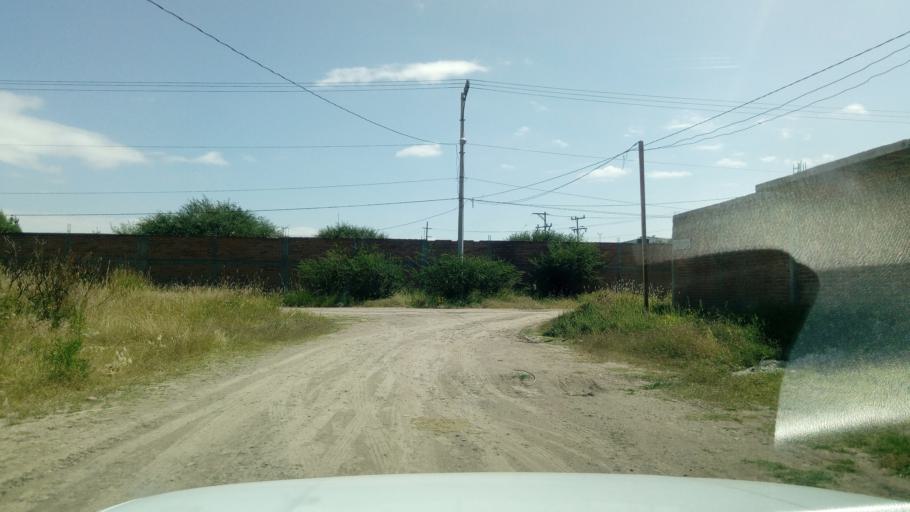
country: MX
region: Durango
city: Victoria de Durango
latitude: 23.9822
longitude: -104.6712
